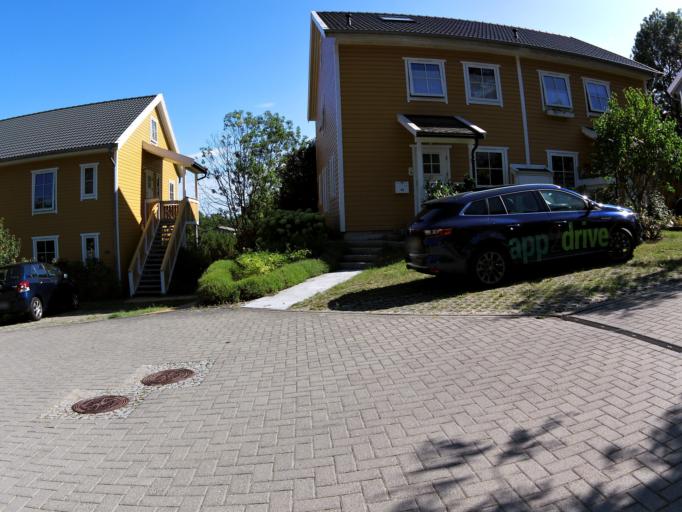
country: DE
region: Mecklenburg-Vorpommern
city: Seebad Bansin
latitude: 53.9652
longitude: 14.1389
